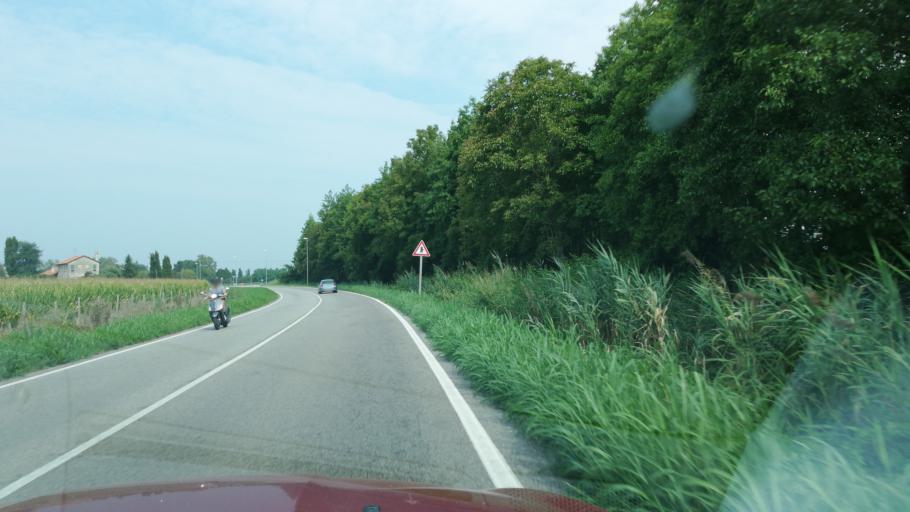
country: IT
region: Veneto
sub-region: Provincia di Venezia
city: San Giorgio di Livenza
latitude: 45.6188
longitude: 12.8014
